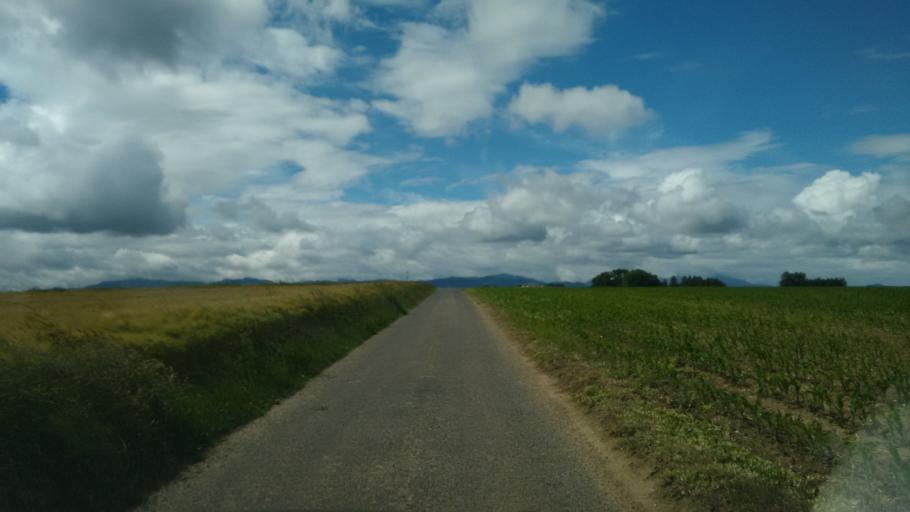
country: AT
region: Upper Austria
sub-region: Politischer Bezirk Steyr-Land
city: Pfarrkirchen bei Bad Hall
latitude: 48.0123
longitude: 14.1657
